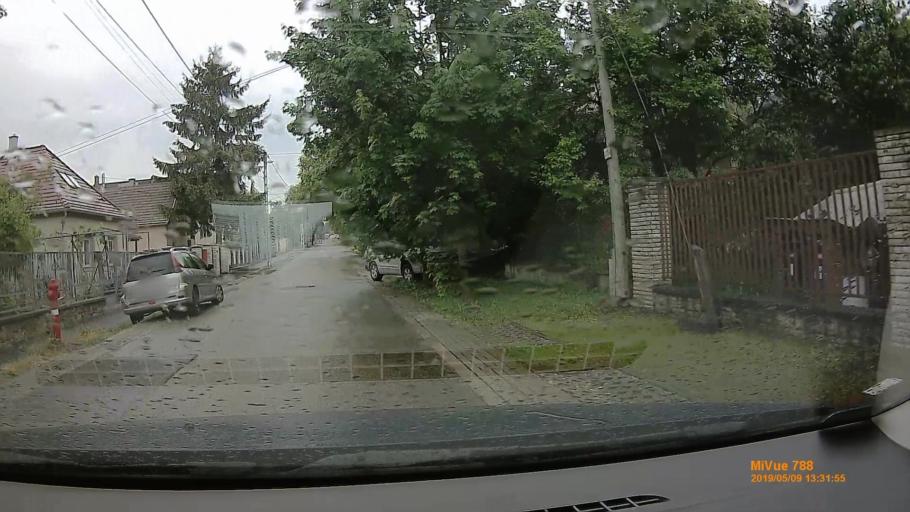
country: HU
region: Budapest
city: Budapest XVI. keruelet
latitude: 47.5344
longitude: 19.2001
